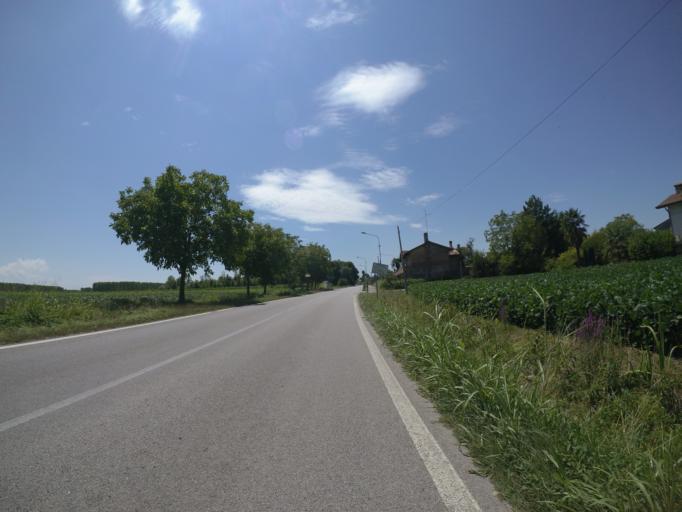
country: IT
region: Friuli Venezia Giulia
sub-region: Provincia di Udine
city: Talmassons
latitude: 45.8845
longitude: 13.1223
